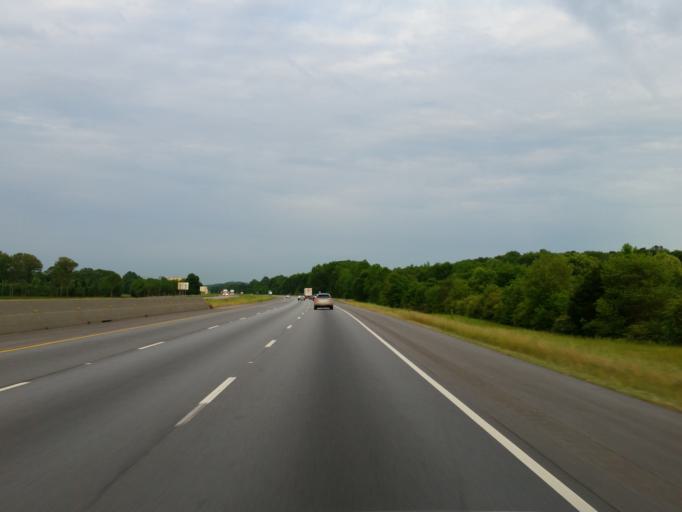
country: US
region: Alabama
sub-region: Calhoun County
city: Oxford
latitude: 33.6050
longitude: -85.8189
